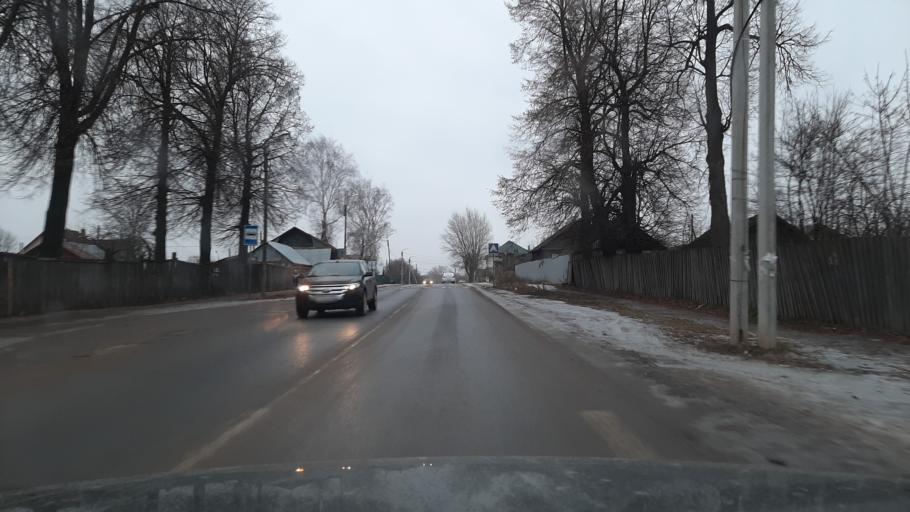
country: RU
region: Ivanovo
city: Shuya
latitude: 56.8623
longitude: 41.3656
